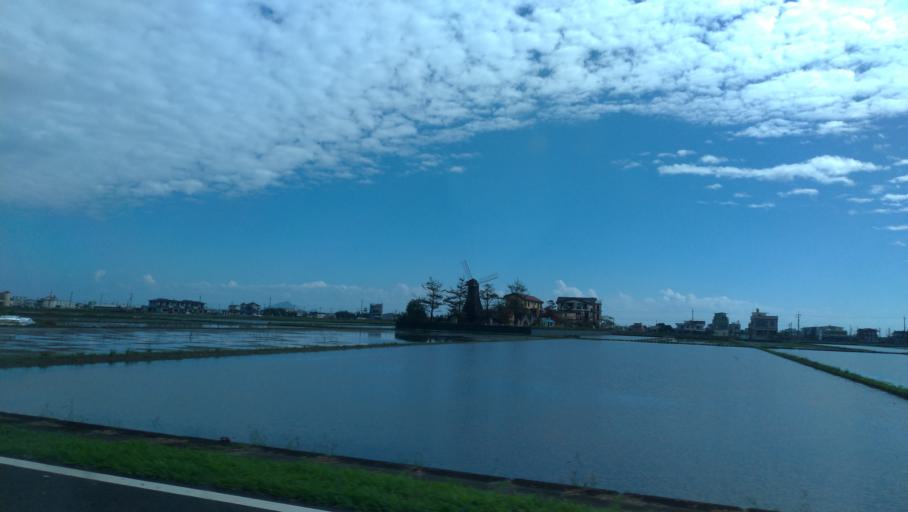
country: TW
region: Taiwan
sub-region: Yilan
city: Yilan
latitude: 24.8003
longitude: 121.7877
